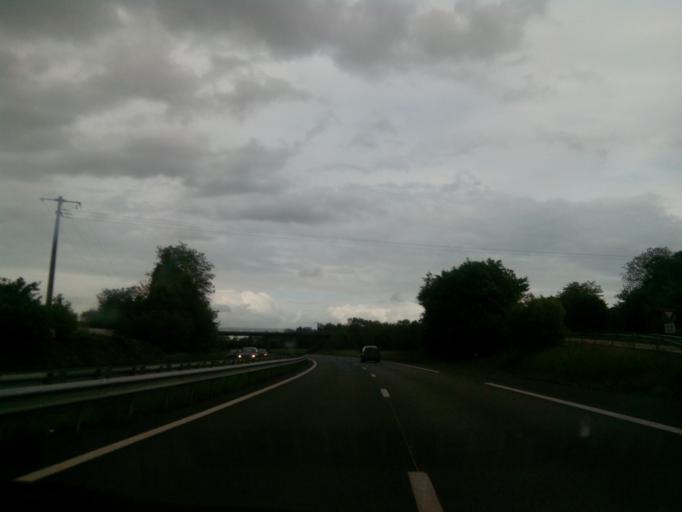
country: FR
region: Brittany
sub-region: Departement d'Ille-et-Vilaine
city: Saint-Thurial
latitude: 48.0453
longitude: -1.9311
